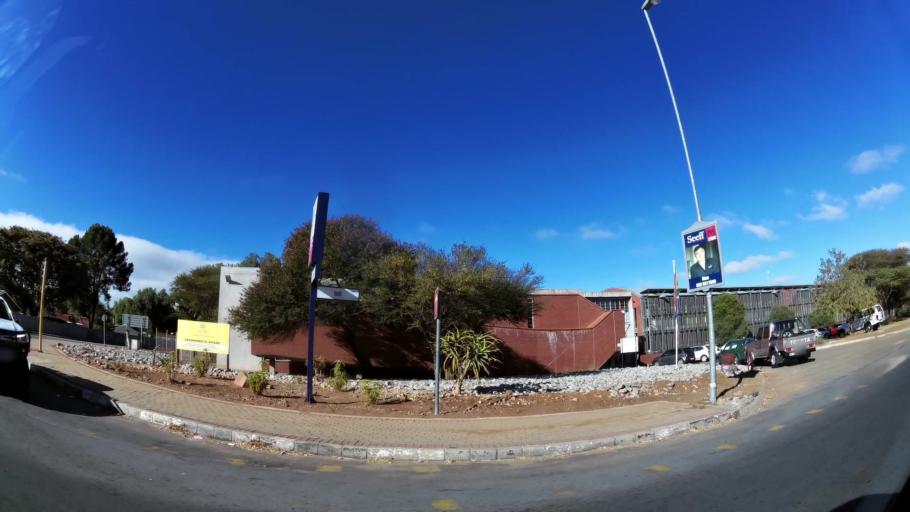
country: ZA
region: Limpopo
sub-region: Capricorn District Municipality
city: Polokwane
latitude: -23.9190
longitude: 29.4618
